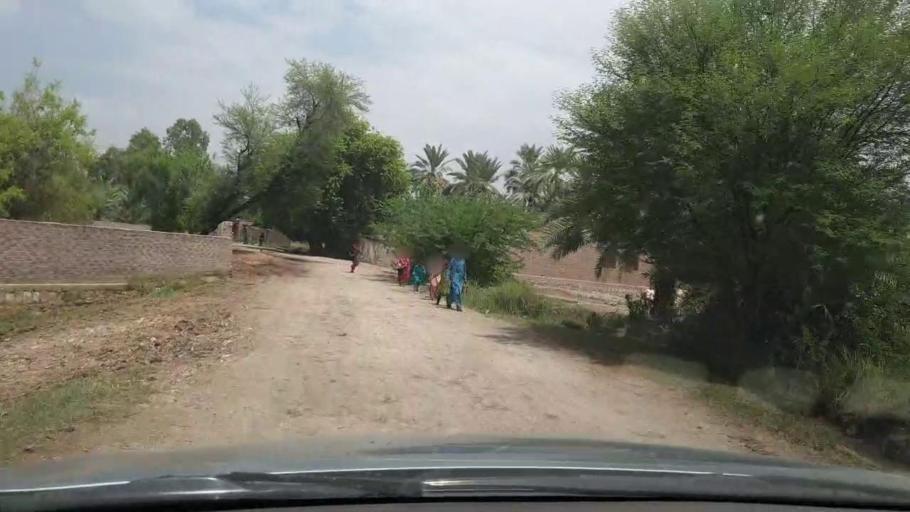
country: PK
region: Sindh
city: Kot Diji
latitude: 27.4187
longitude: 68.7619
